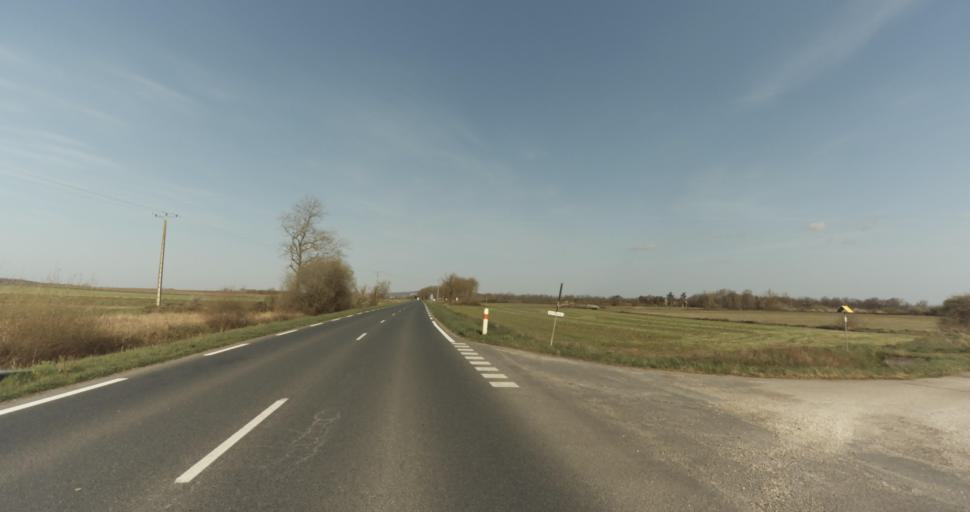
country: FR
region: Midi-Pyrenees
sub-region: Departement du Tarn
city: Saint-Sulpice-la-Pointe
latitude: 43.7526
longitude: 1.7237
